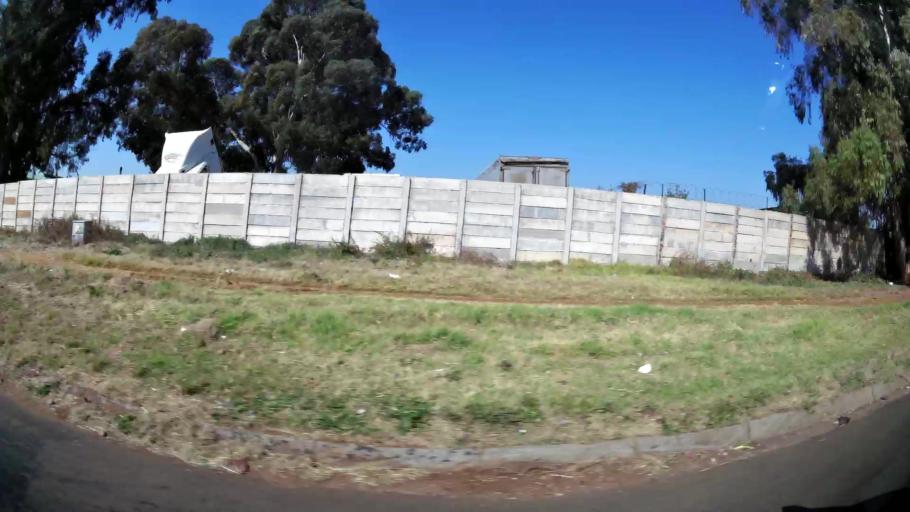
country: ZA
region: Gauteng
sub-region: Ekurhuleni Metropolitan Municipality
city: Boksburg
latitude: -26.1728
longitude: 28.2172
